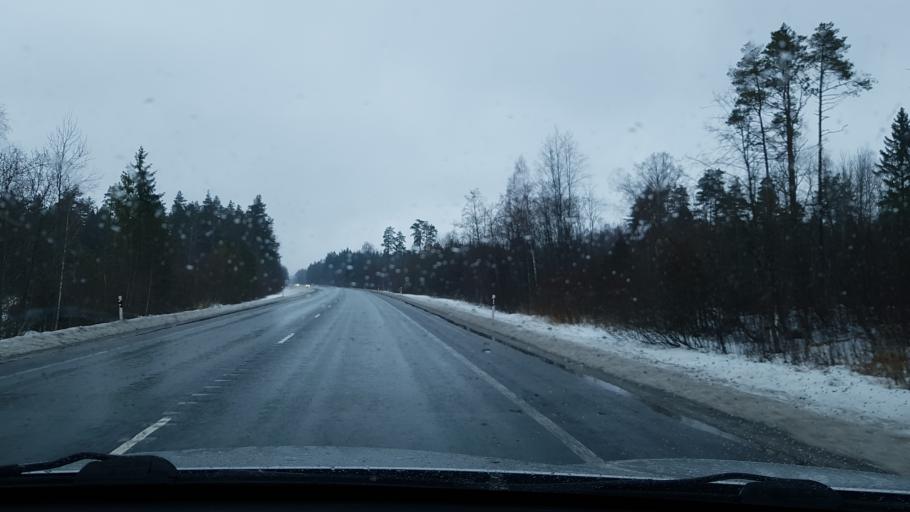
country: EE
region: Raplamaa
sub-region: Kohila vald
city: Kohila
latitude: 59.1404
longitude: 24.7903
